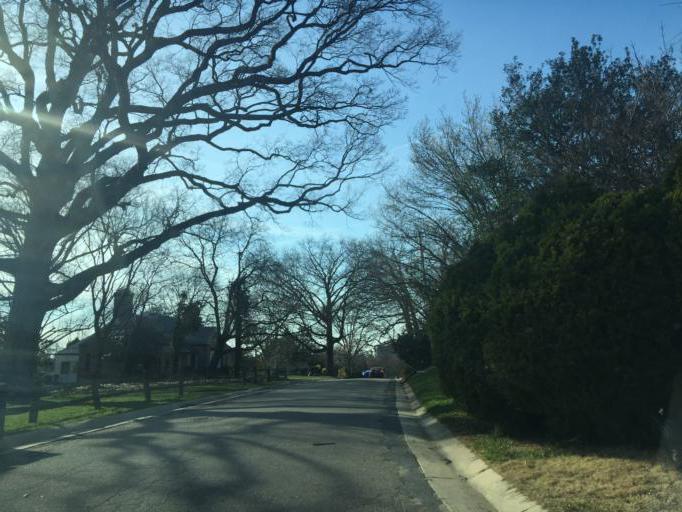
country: US
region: Maryland
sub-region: Baltimore County
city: Towson
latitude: 39.3907
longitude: -76.5910
